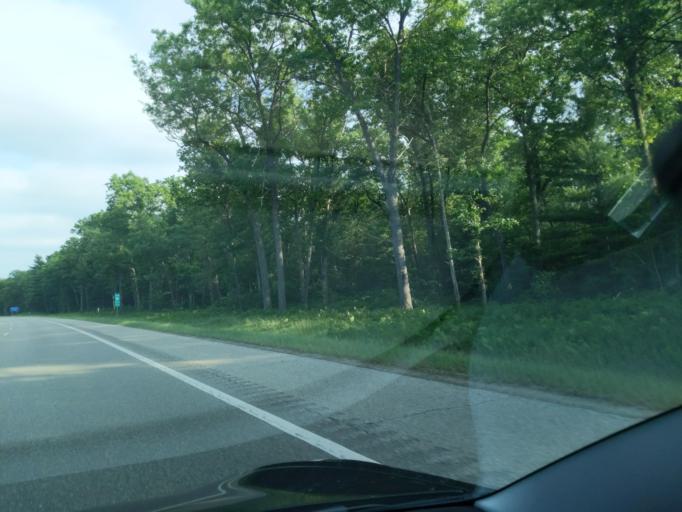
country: US
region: Michigan
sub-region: Muskegon County
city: Lakewood Club
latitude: 43.3677
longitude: -86.2730
